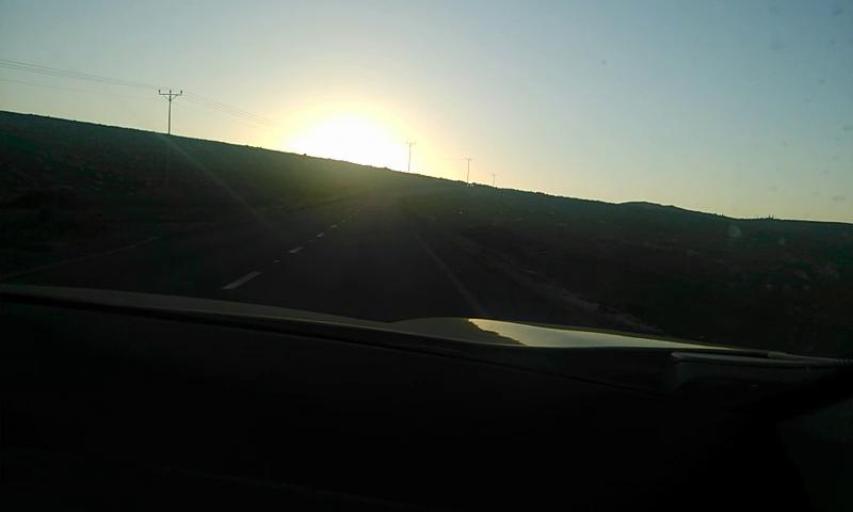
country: PS
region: West Bank
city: Rammun
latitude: 31.9184
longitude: 35.3334
